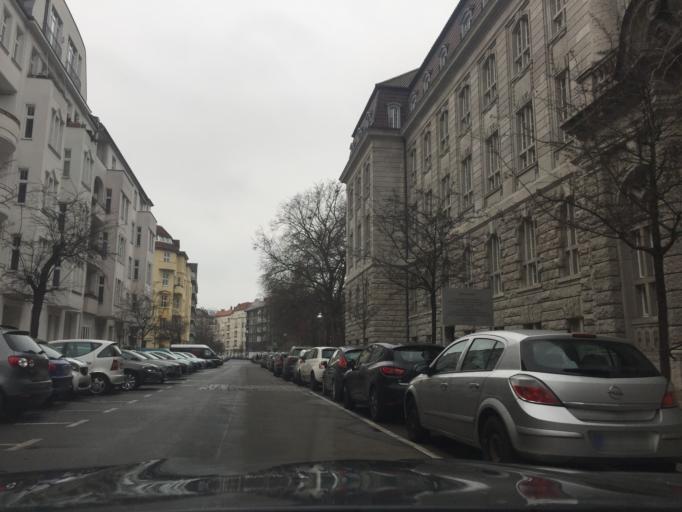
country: DE
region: Berlin
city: Charlottenburg Bezirk
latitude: 52.5095
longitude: 13.2945
